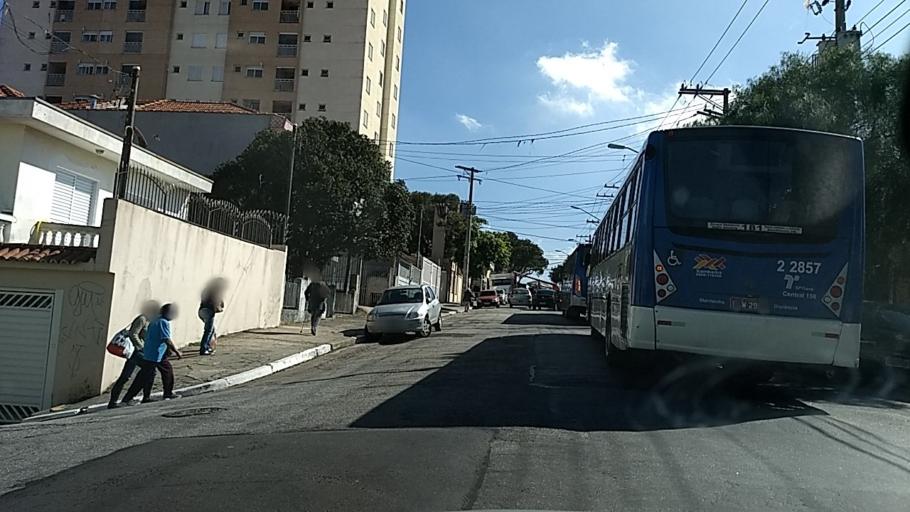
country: BR
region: Sao Paulo
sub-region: Guarulhos
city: Guarulhos
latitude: -23.4888
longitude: -46.5820
